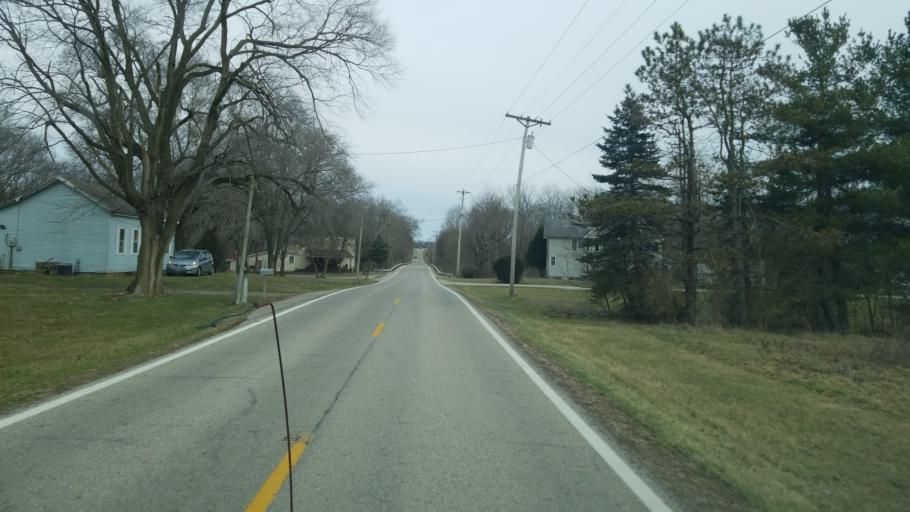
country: US
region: Ohio
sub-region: Pickaway County
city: Williamsport
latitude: 39.5508
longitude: -83.1099
